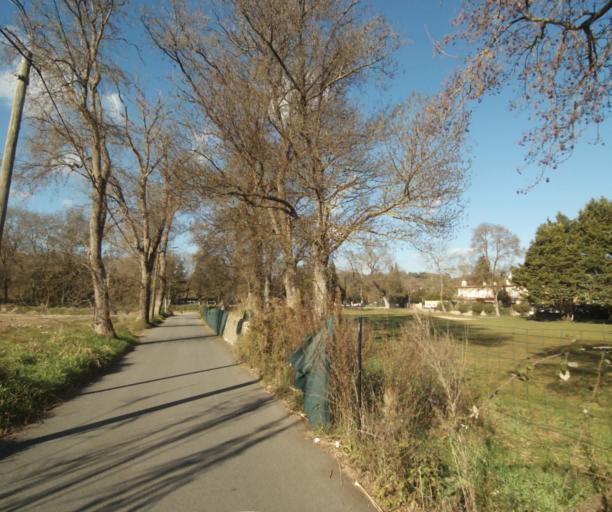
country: FR
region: Provence-Alpes-Cote d'Azur
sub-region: Departement des Alpes-Maritimes
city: Biot
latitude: 43.6167
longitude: 7.1032
